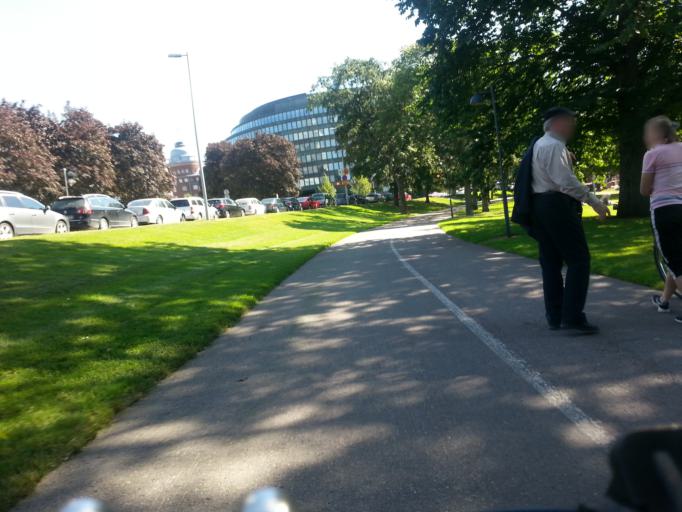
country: FI
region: Uusimaa
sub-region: Helsinki
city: Helsinki
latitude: 60.1808
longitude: 24.9456
